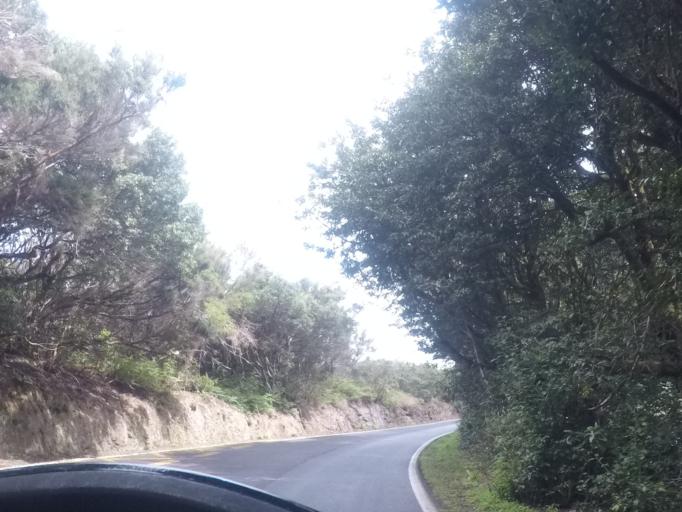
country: ES
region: Canary Islands
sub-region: Provincia de Santa Cruz de Tenerife
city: Santa Cruz de Tenerife
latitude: 28.5393
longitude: -16.2328
